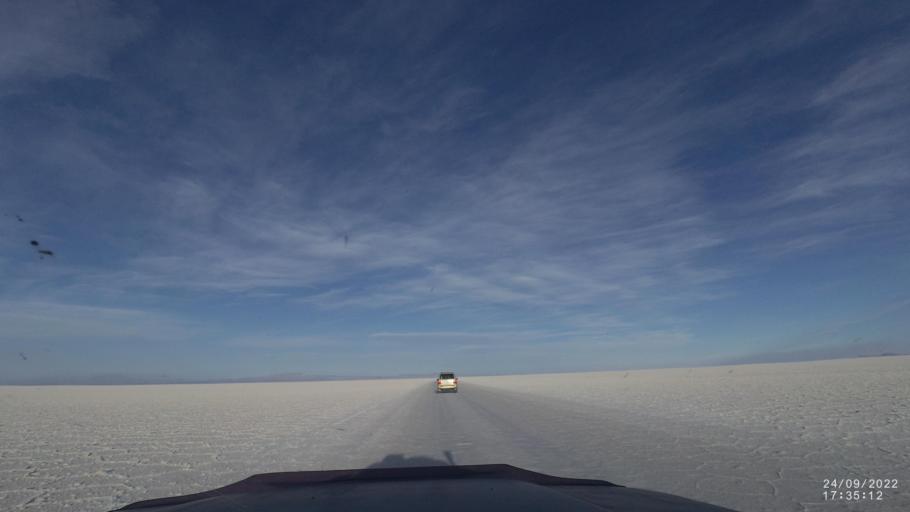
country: BO
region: Potosi
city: Colchani
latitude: -20.3230
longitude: -67.2631
